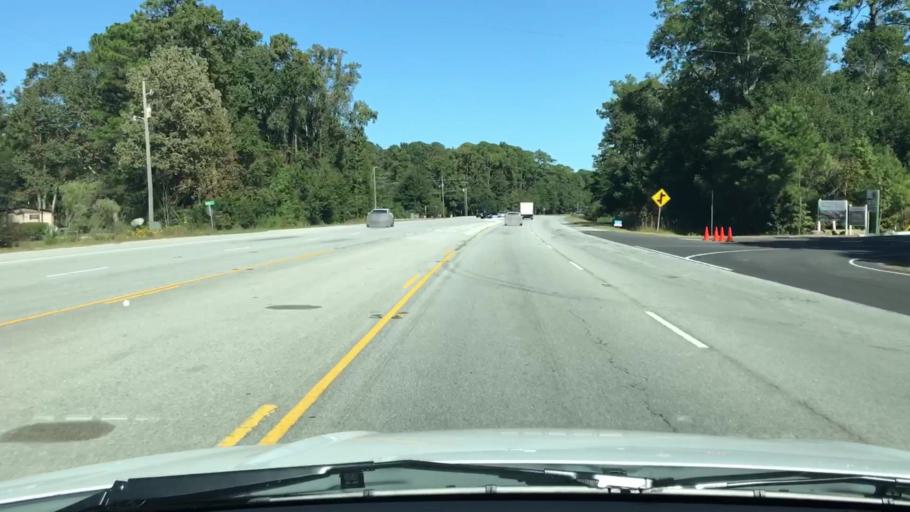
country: US
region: South Carolina
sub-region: Beaufort County
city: Burton
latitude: 32.4149
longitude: -80.7484
